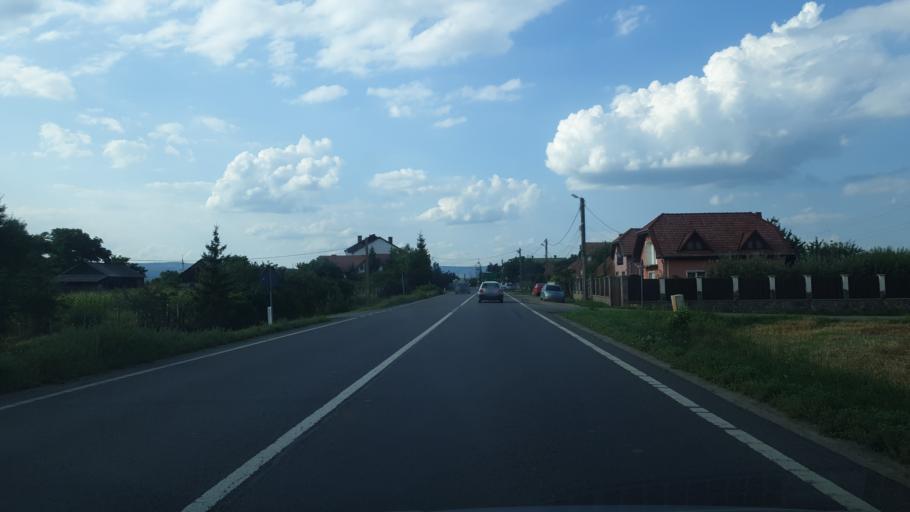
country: RO
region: Covasna
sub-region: Municipiul Sfantu Gheorghe
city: Sfantu-Gheorghe
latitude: 45.8341
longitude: 25.8045
